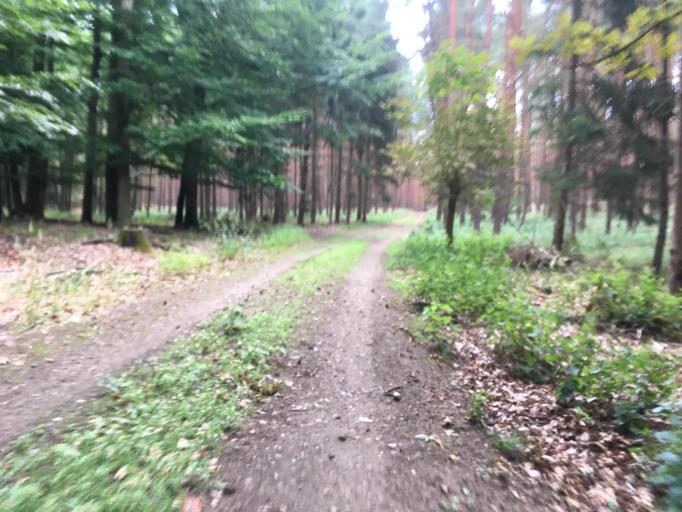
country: DE
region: Brandenburg
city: Althuttendorf
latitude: 52.9947
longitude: 13.8022
